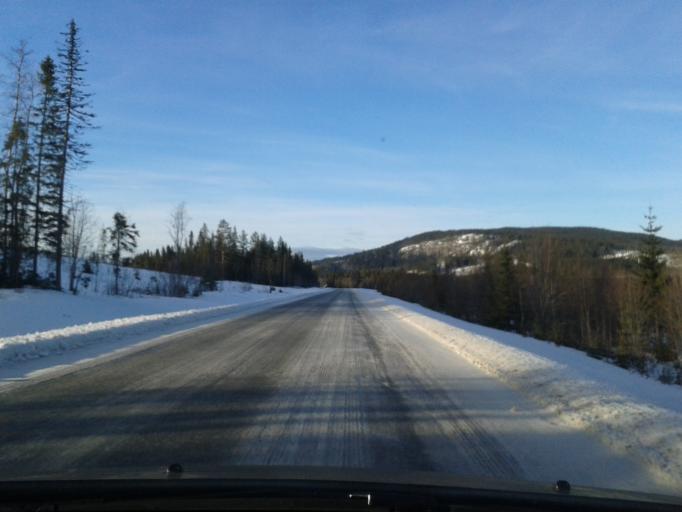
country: SE
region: Vaesterbotten
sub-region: Asele Kommun
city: Asele
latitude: 63.7772
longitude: 17.6700
